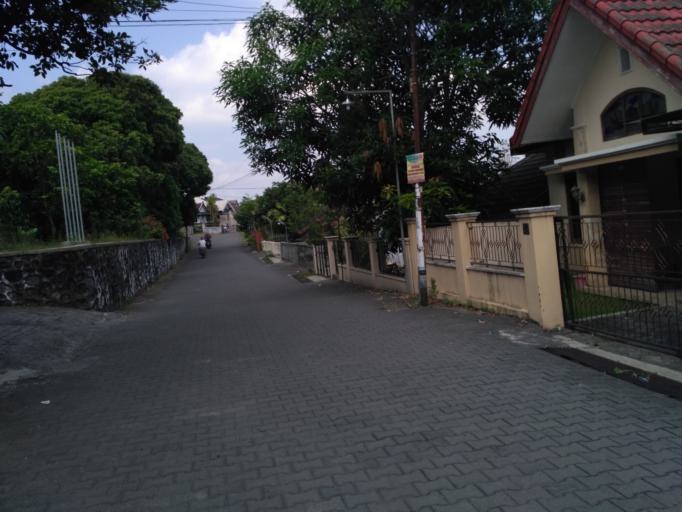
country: ID
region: Daerah Istimewa Yogyakarta
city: Depok
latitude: -7.7417
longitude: 110.4101
